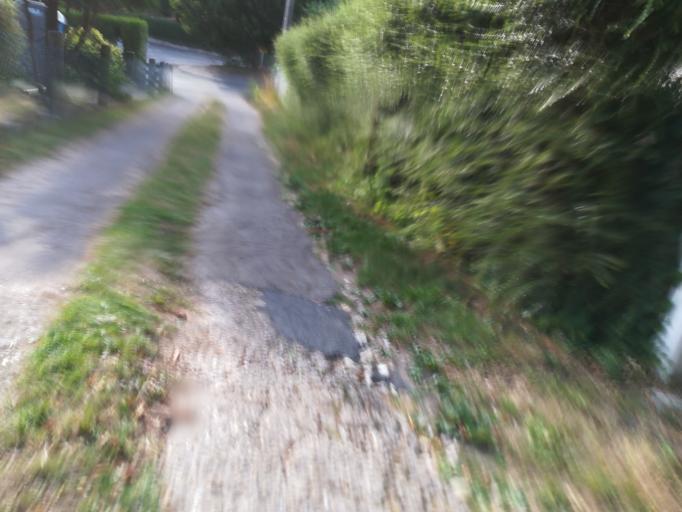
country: FR
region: Haute-Normandie
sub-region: Departement de la Seine-Maritime
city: Mont-Saint-Aignan
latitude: 49.4641
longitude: 1.0899
